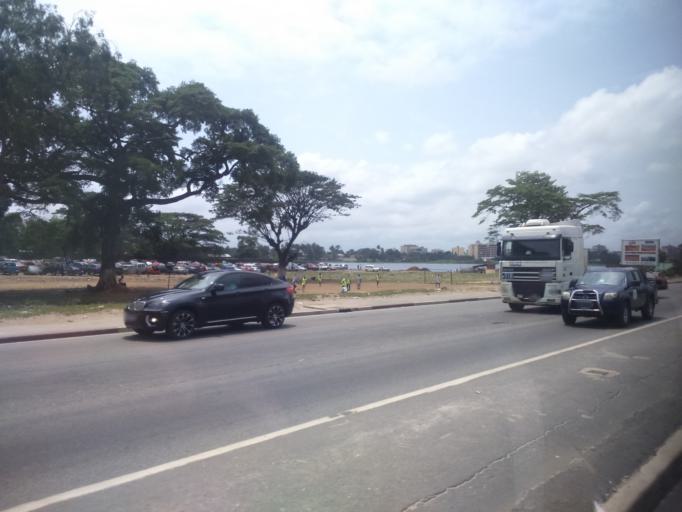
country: CI
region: Lagunes
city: Abidjan
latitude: 5.3104
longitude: -4.0044
